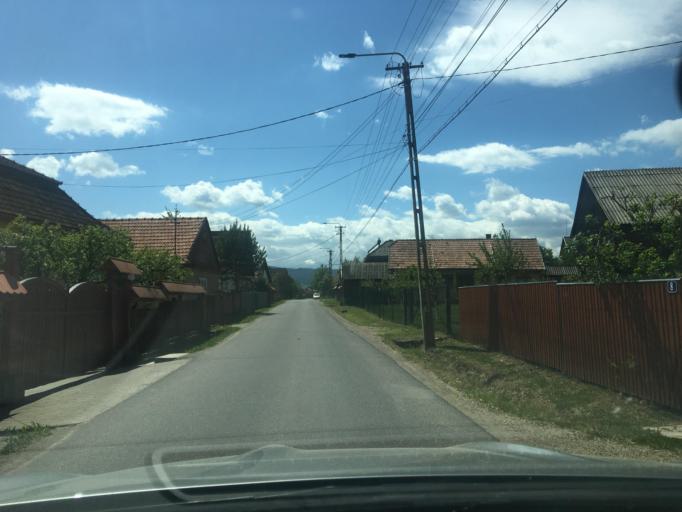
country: RO
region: Harghita
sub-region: Comuna Remetea
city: Remetea
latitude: 46.8053
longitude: 25.4590
